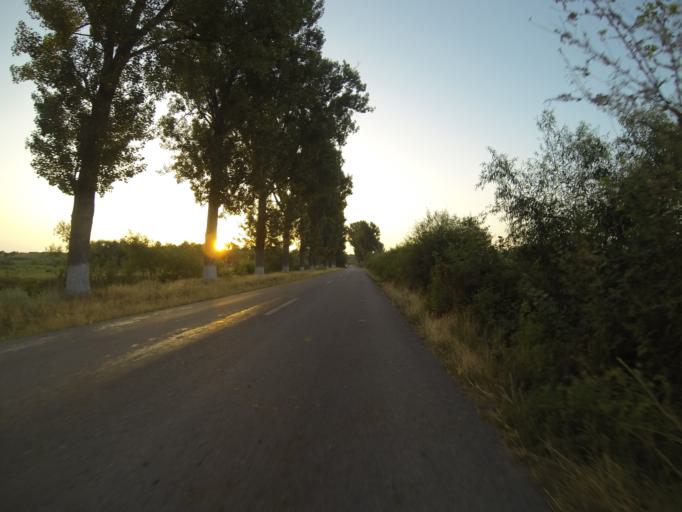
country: RO
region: Dolj
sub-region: Comuna Dobresti
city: Dobresti
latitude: 43.9826
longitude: 23.9359
